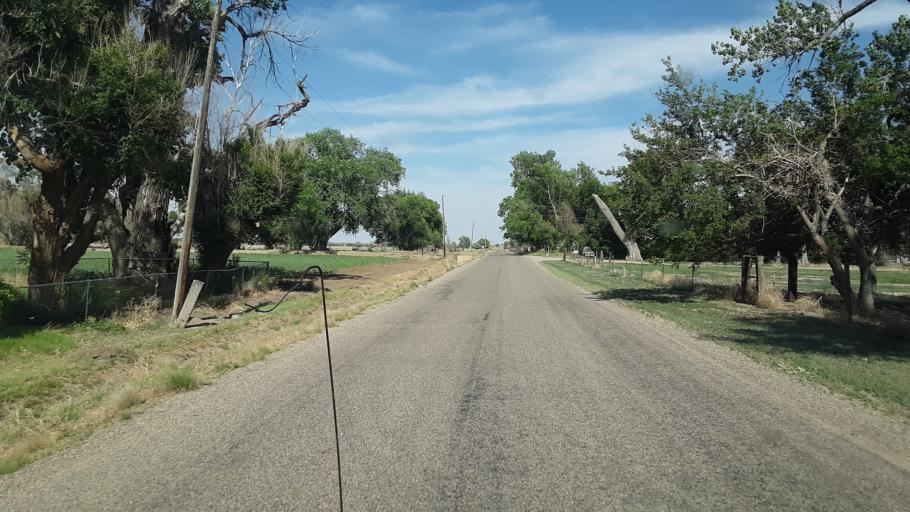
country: US
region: Colorado
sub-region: Otero County
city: Fowler
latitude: 38.1632
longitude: -103.9141
